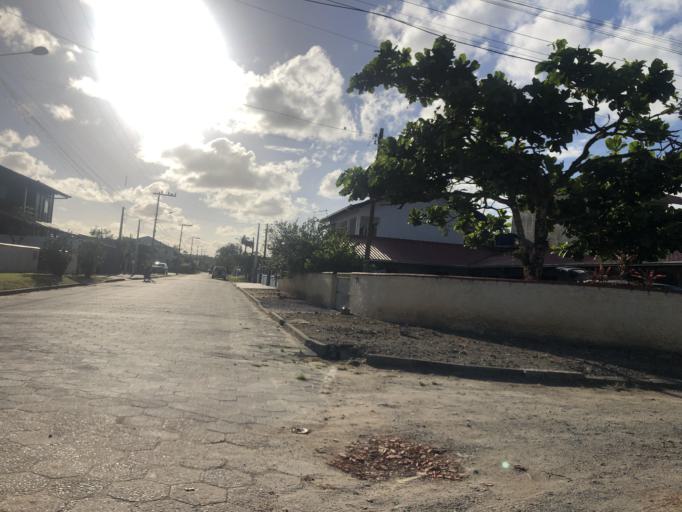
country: BR
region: Santa Catarina
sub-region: Sao Francisco Do Sul
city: Sao Francisco do Sul
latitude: -26.2167
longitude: -48.5312
